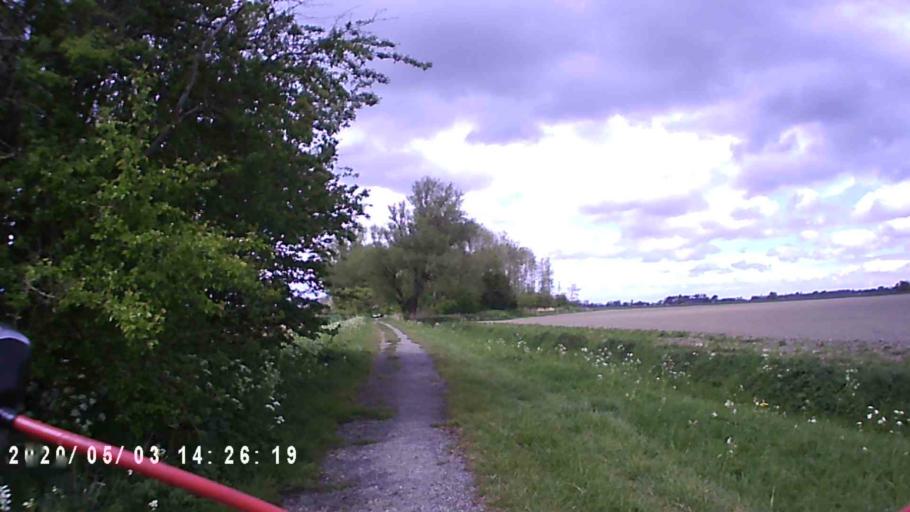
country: NL
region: Groningen
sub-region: Gemeente Zuidhorn
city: Oldehove
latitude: 53.3404
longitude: 6.3962
